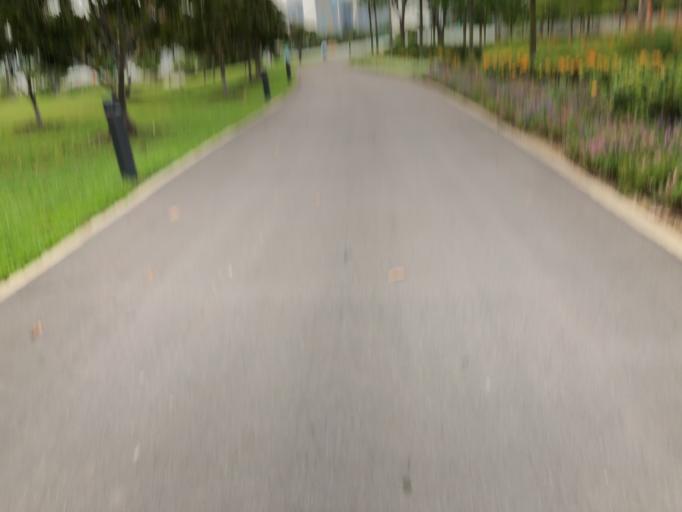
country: SG
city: Singapore
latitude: 1.2835
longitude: 103.8737
